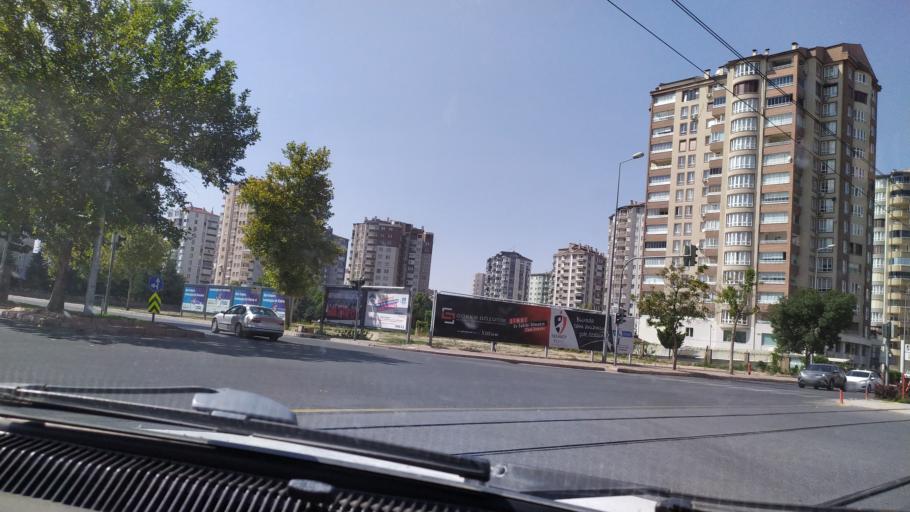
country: TR
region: Kayseri
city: Kayseri
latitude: 38.7279
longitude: 35.5257
